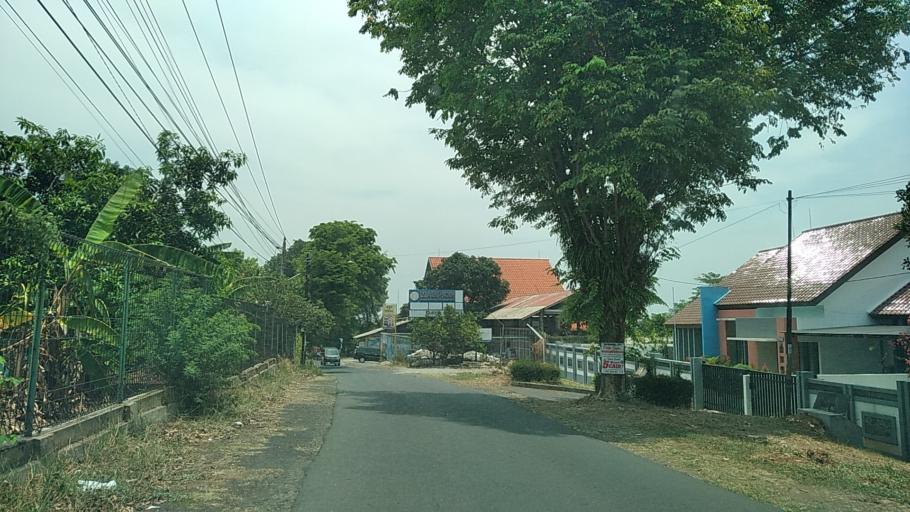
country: ID
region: Central Java
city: Semarang
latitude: -7.0501
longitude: 110.4137
